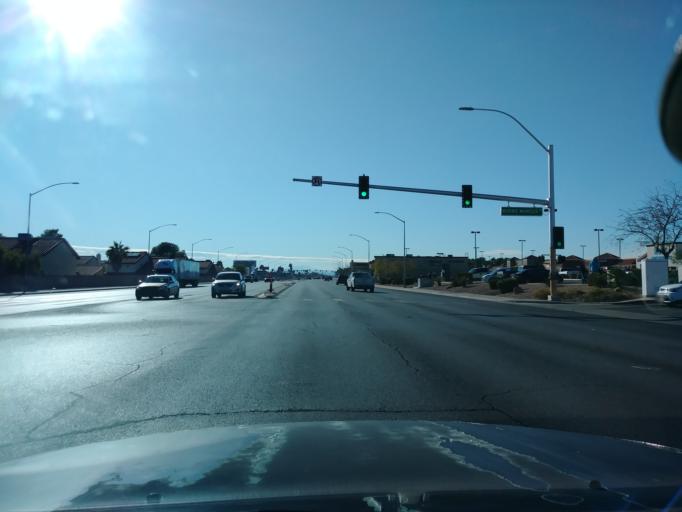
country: US
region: Nevada
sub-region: Clark County
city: Spring Valley
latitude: 36.1630
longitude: -115.2441
